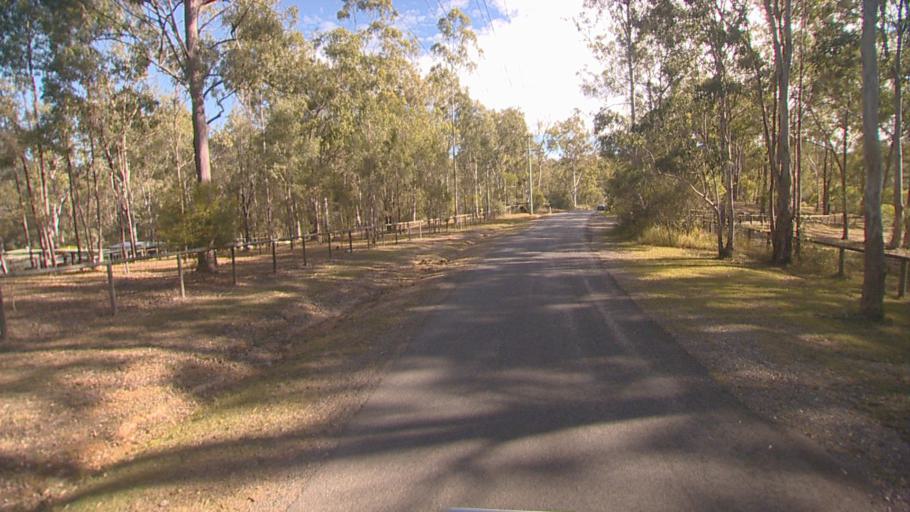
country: AU
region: Queensland
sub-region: Logan
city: Cedar Vale
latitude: -27.8361
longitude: 153.0707
